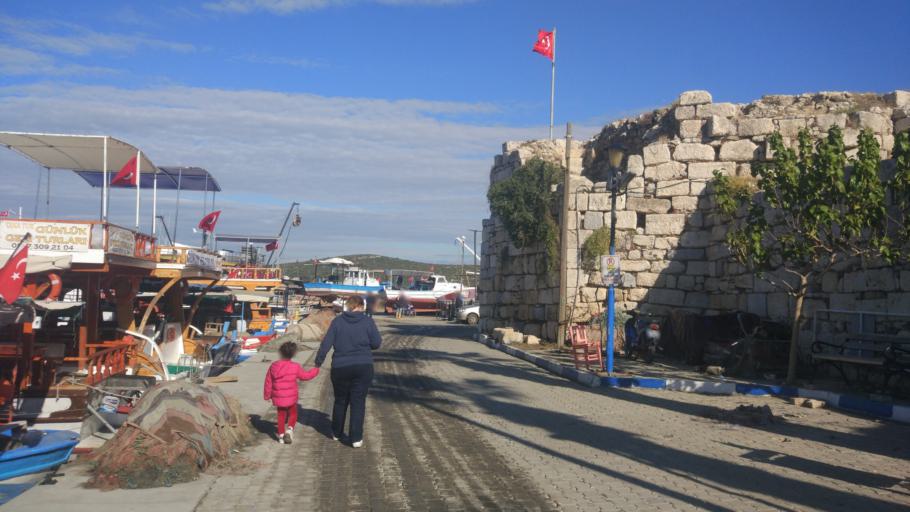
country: TR
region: Izmir
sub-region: Seferihisar
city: Seferhisar
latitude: 38.1944
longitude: 26.7842
